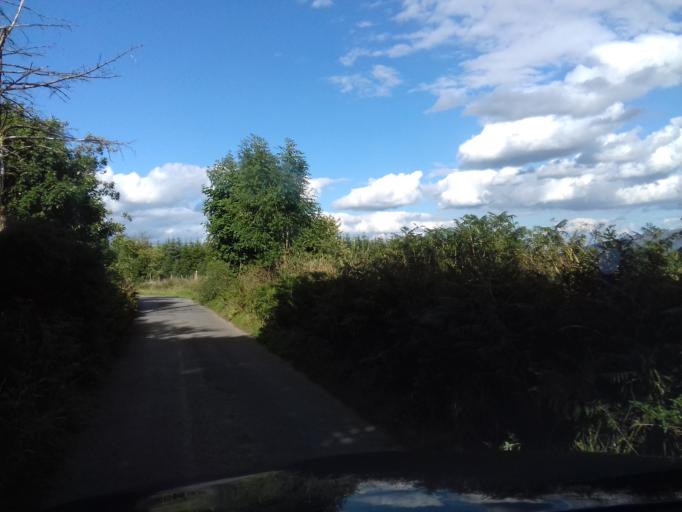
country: IE
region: Leinster
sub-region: Kilkenny
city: Graiguenamanagh
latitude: 52.5631
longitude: -7.0062
